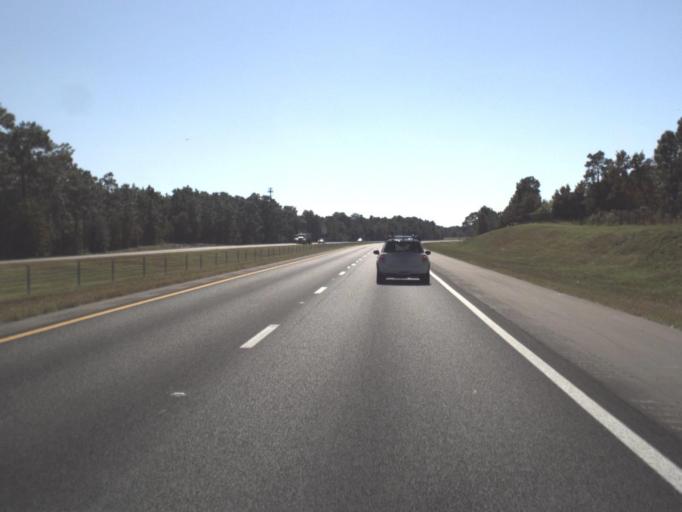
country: US
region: Florida
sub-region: Hernando County
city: Brookridge
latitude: 28.5175
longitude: -82.4777
